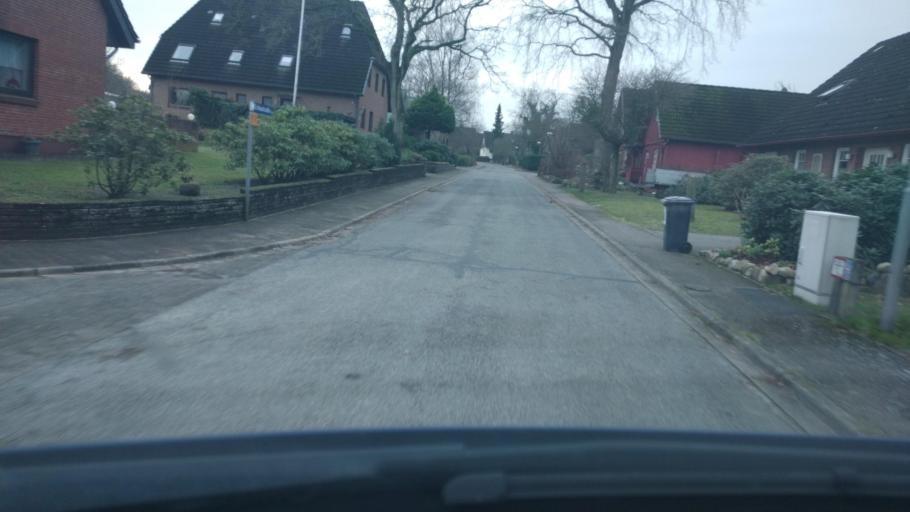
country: DE
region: Schleswig-Holstein
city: Neuberend
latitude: 54.5502
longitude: 9.5304
